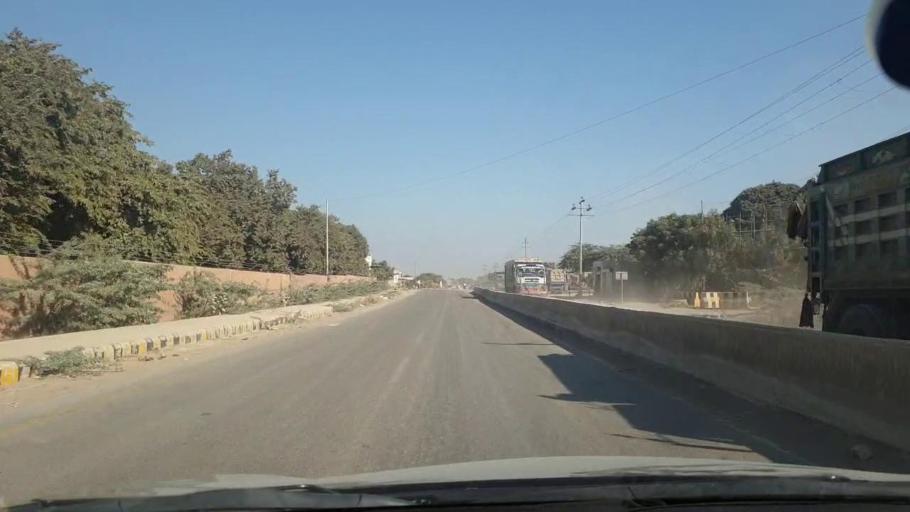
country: PK
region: Sindh
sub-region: Karachi District
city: Karachi
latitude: 25.0898
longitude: 67.0131
